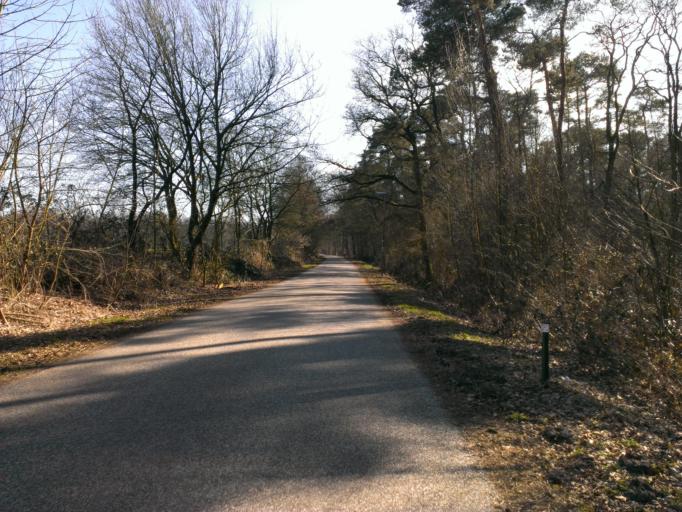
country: NL
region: Overijssel
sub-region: Gemeente Almelo
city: Almelo
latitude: 52.3347
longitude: 6.6792
